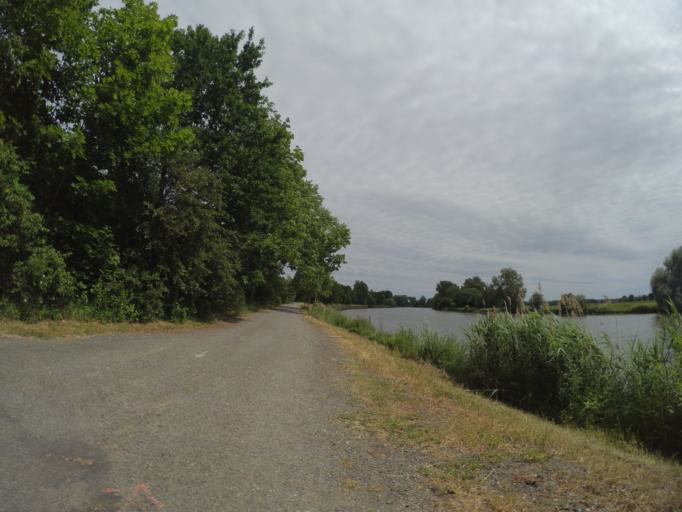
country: CZ
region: Central Bohemia
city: Lysa nad Labem
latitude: 50.1728
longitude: 14.8729
